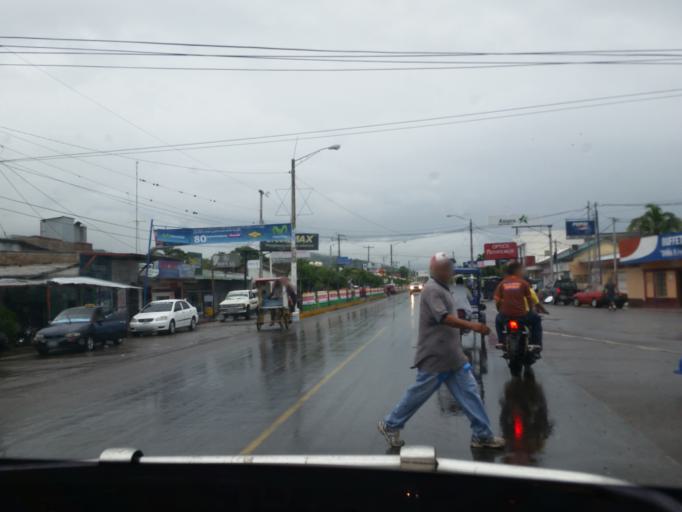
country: NI
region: Matagalpa
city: Ciudad Dario
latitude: 12.8520
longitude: -86.0987
